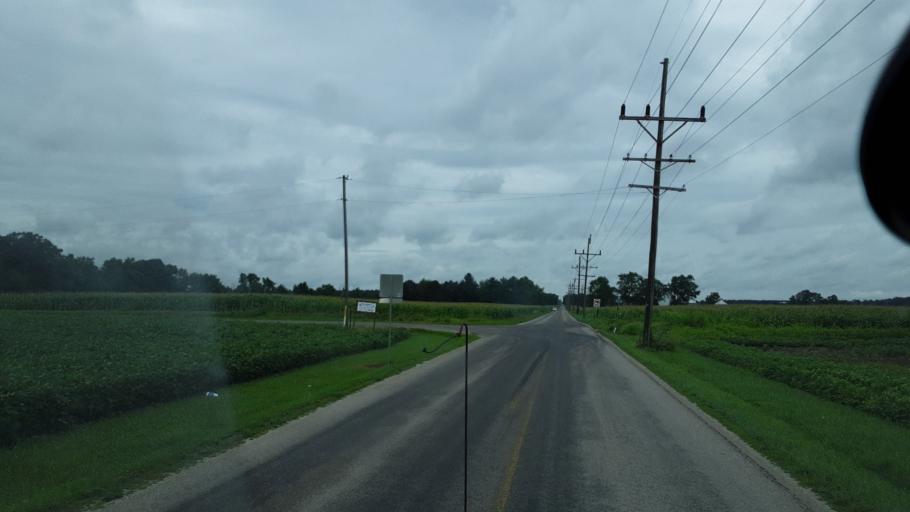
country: US
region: Indiana
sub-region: Jay County
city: Portland
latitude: 40.4455
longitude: -85.0199
